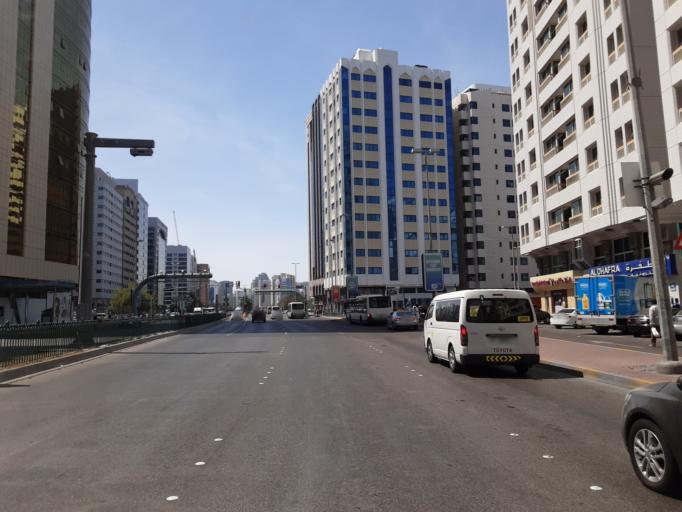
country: AE
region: Abu Dhabi
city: Abu Dhabi
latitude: 24.4882
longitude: 54.3642
